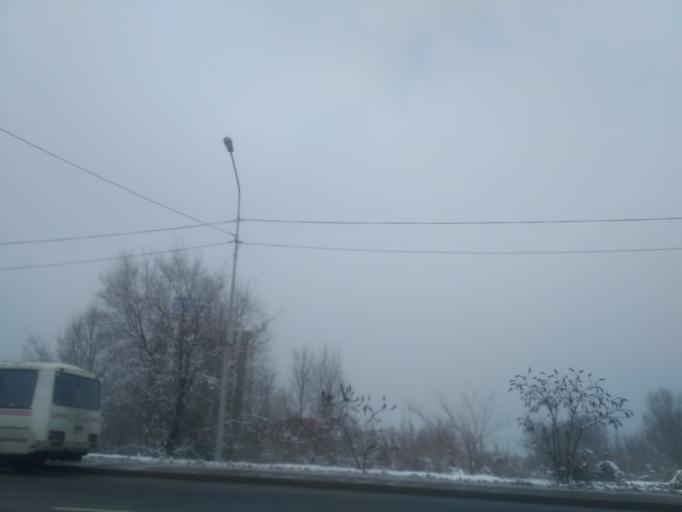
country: KZ
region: Almaty Qalasy
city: Almaty
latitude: 43.2266
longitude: 76.9416
